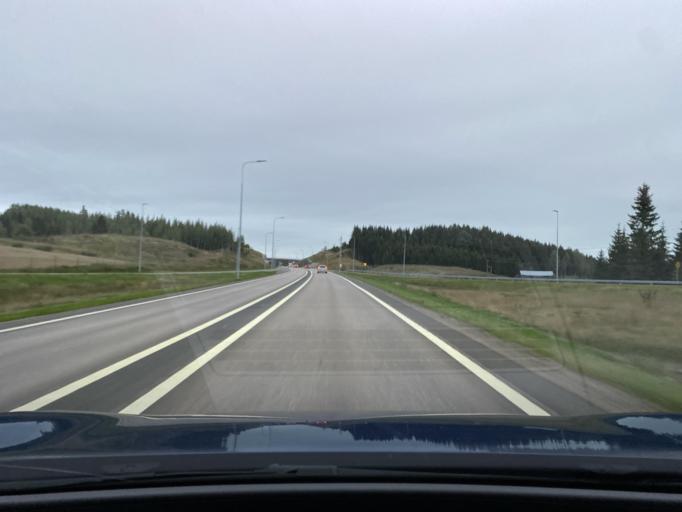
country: FI
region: Paijanne Tavastia
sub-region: Lahti
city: Hollola
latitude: 60.9611
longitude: 25.5323
